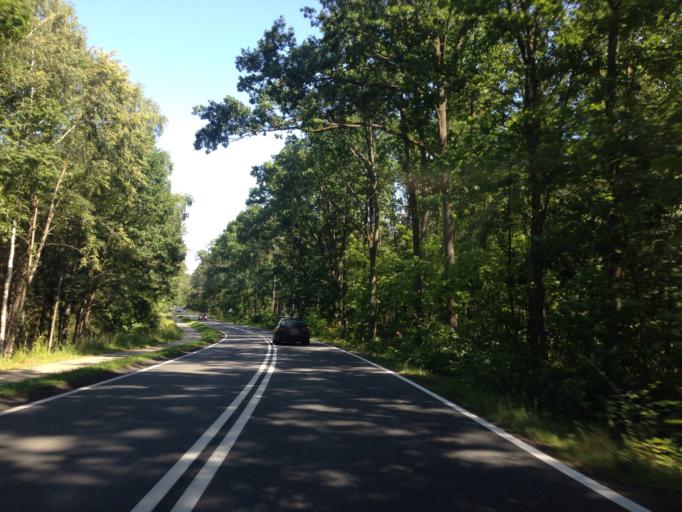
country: PL
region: Kujawsko-Pomorskie
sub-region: Powiat swiecki
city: Osie
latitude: 53.6061
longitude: 18.3205
